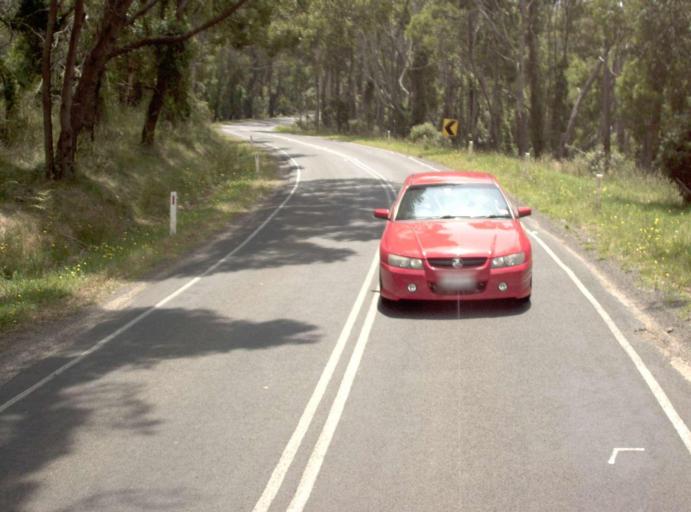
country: AU
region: Victoria
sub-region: Latrobe
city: Traralgon
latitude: -38.3898
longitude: 146.7529
